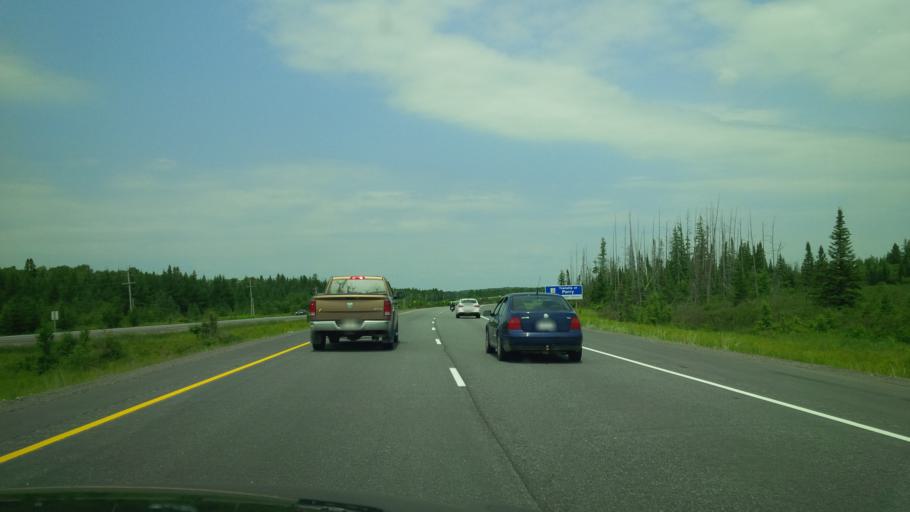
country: CA
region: Ontario
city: Huntsville
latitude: 45.4364
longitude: -79.2423
